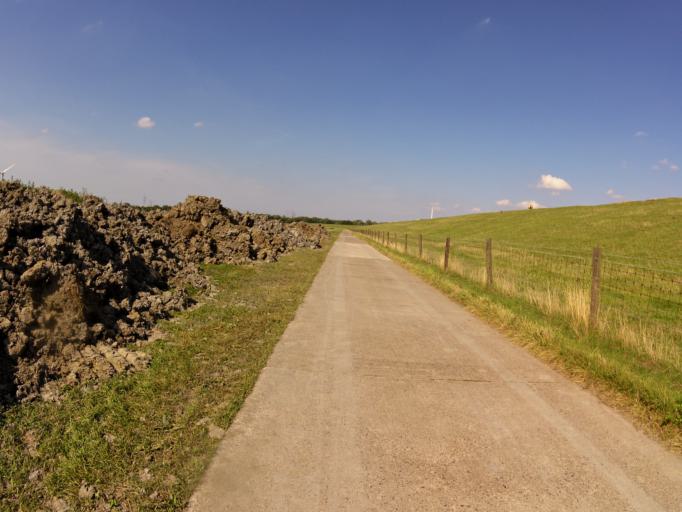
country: DE
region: Lower Saxony
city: Nordenham
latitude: 53.4155
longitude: 8.4720
